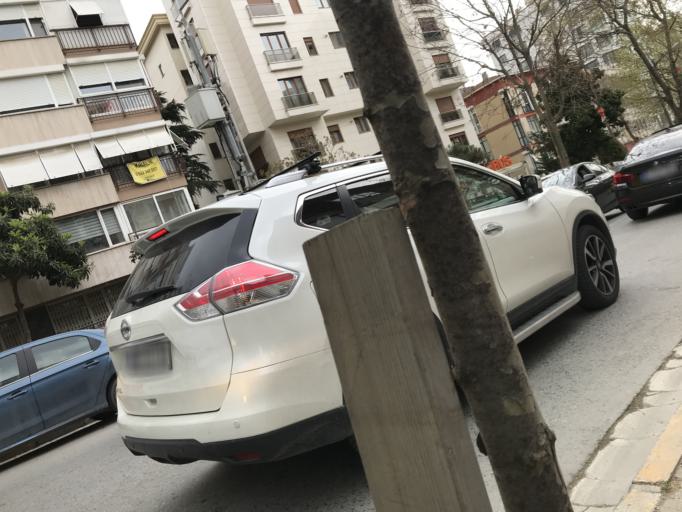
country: TR
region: Istanbul
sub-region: Atasehir
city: Atasehir
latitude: 40.9750
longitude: 29.0636
